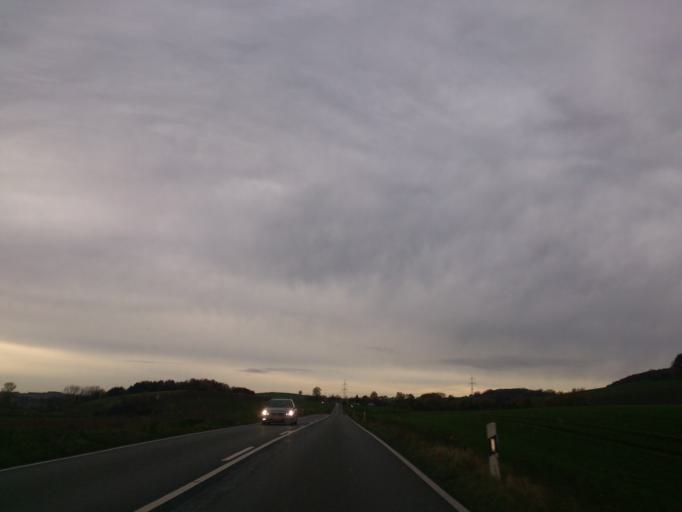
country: DE
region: North Rhine-Westphalia
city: Brakel
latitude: 51.7137
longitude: 9.2677
